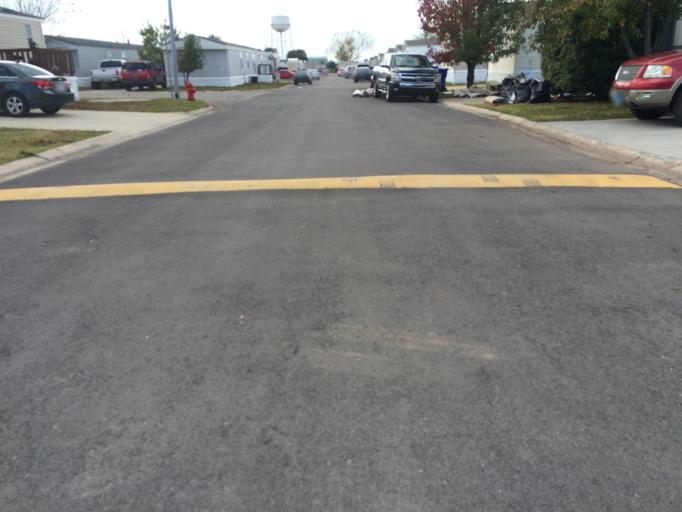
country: US
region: Oklahoma
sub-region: Cleveland County
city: Norman
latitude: 35.2416
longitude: -97.4517
